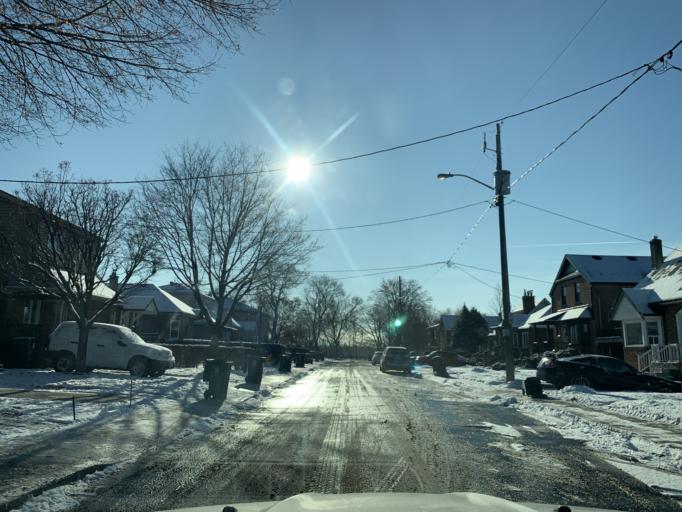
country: CA
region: Ontario
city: Toronto
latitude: 43.6814
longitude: -79.4886
